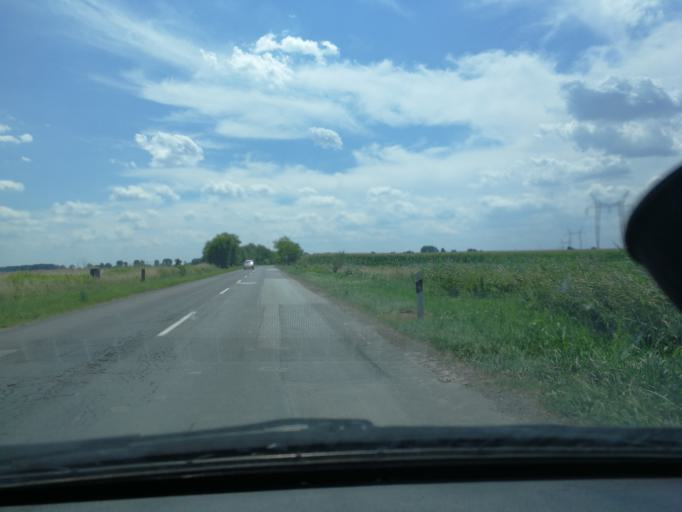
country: HU
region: Bacs-Kiskun
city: Tass
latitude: 47.0445
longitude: 19.0233
